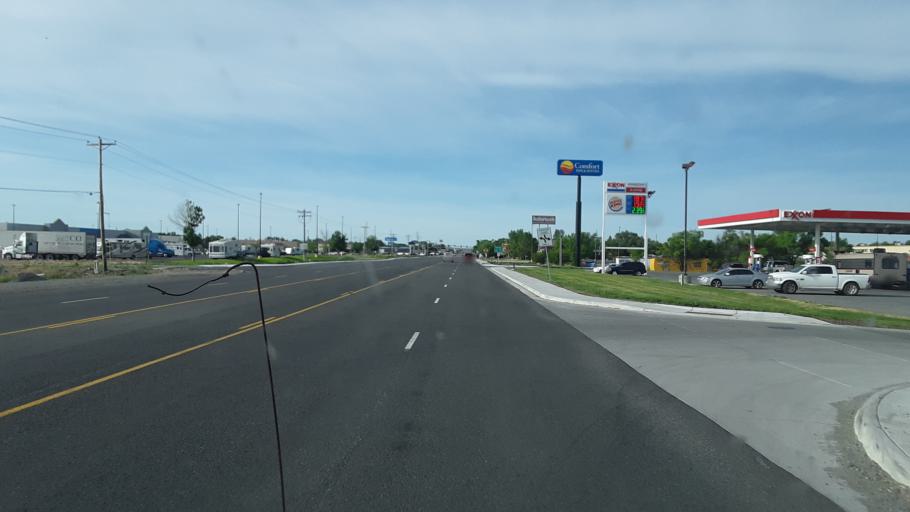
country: US
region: Wyoming
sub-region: Fremont County
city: Riverton
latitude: 43.0455
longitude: -108.3808
